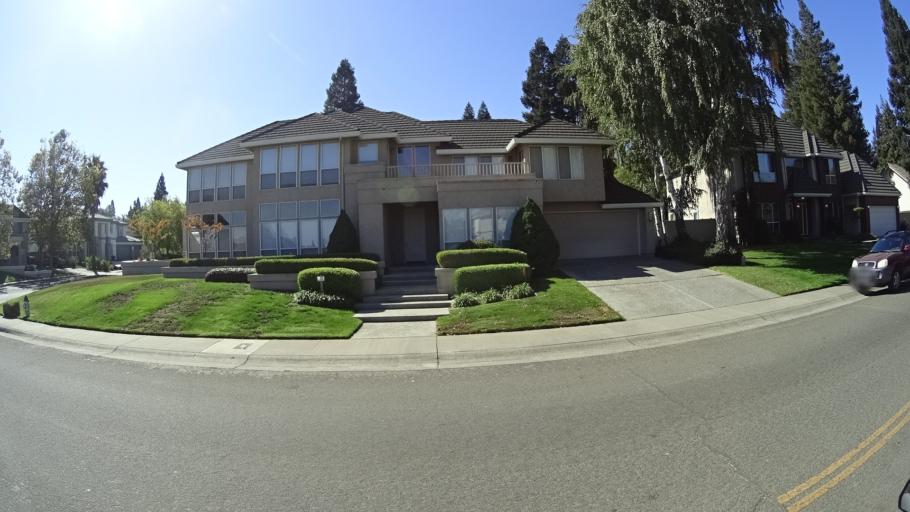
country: US
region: California
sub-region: Sacramento County
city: Parkway
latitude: 38.4786
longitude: -121.5316
